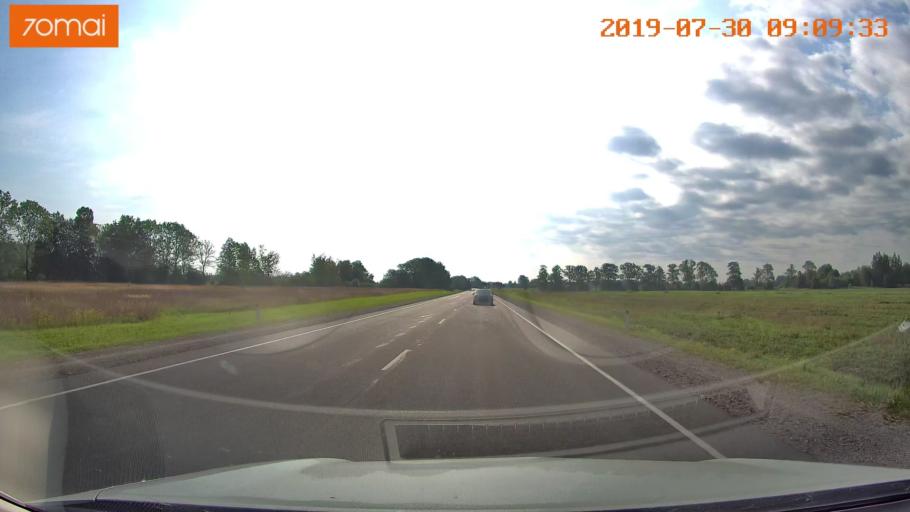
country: RU
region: Kaliningrad
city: Nesterov
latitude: 54.6133
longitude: 22.4103
